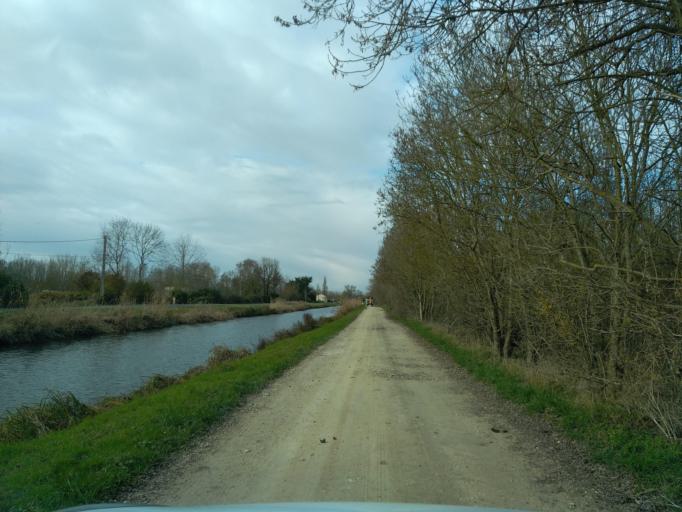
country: FR
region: Pays de la Loire
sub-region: Departement de la Vendee
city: Maillezais
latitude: 46.3153
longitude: -0.7737
